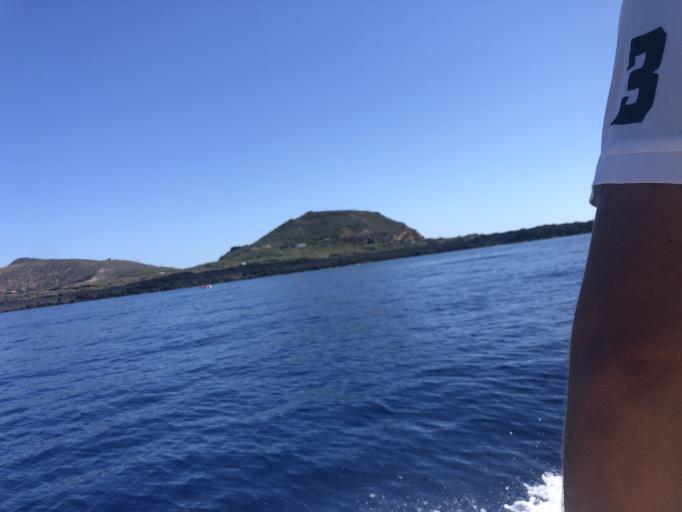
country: IT
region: Sicily
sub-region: Agrigento
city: Lampedusa
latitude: 35.8736
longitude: 12.8508
